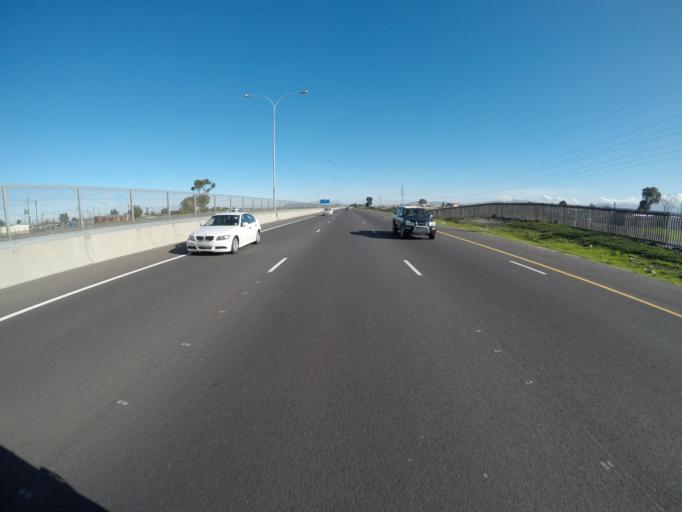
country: ZA
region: Western Cape
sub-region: City of Cape Town
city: Lansdowne
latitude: -33.9889
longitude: 18.6457
